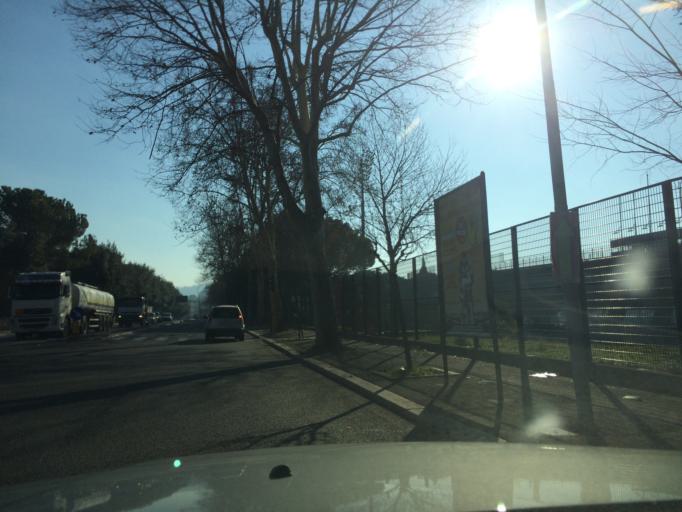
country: IT
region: Umbria
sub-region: Provincia di Terni
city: Terni
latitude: 42.5629
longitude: 12.6367
